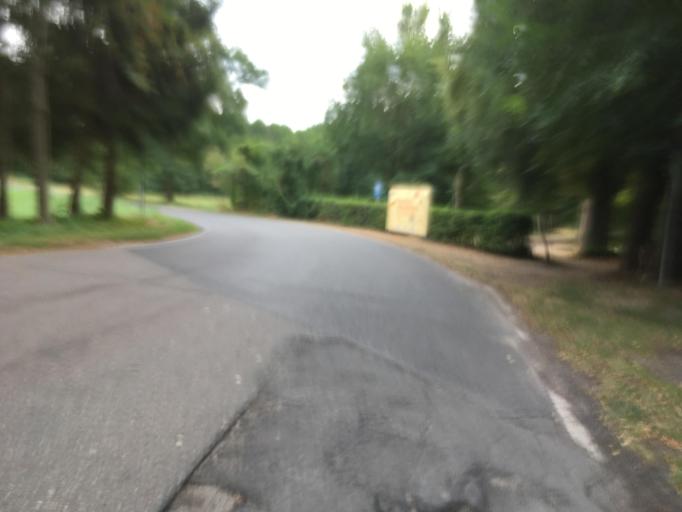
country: DE
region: Brandenburg
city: Lychen
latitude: 53.1718
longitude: 13.2363
